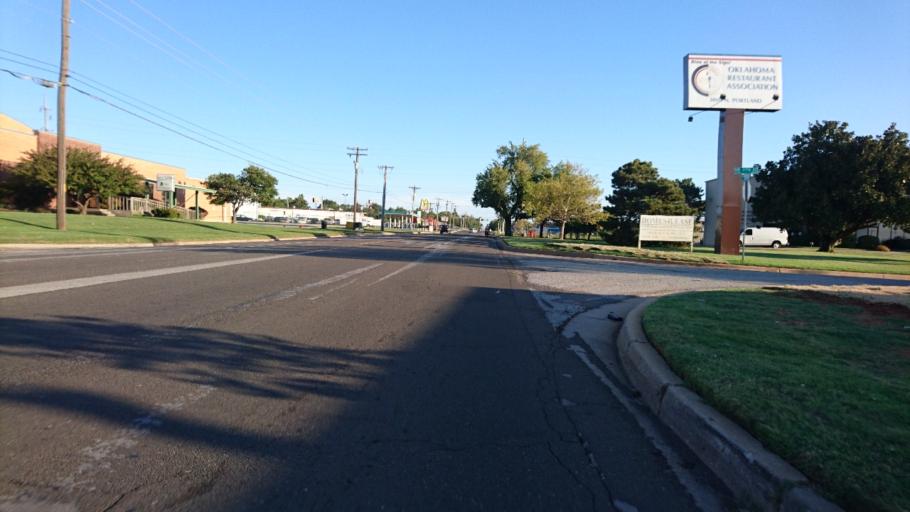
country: US
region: Oklahoma
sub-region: Oklahoma County
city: Warr Acres
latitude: 35.5089
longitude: -97.5833
